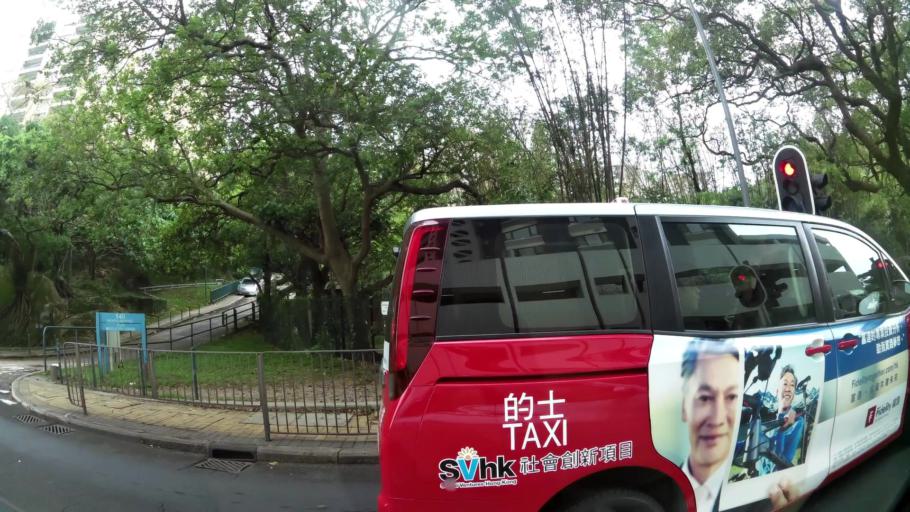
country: HK
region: Central and Western
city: Central
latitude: 22.2639
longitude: 114.1340
